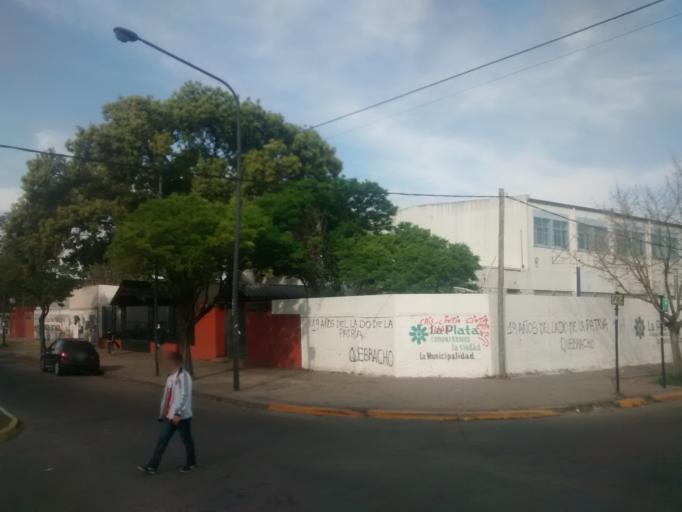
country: AR
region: Buenos Aires
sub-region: Partido de La Plata
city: La Plata
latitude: -34.9333
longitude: -57.9387
